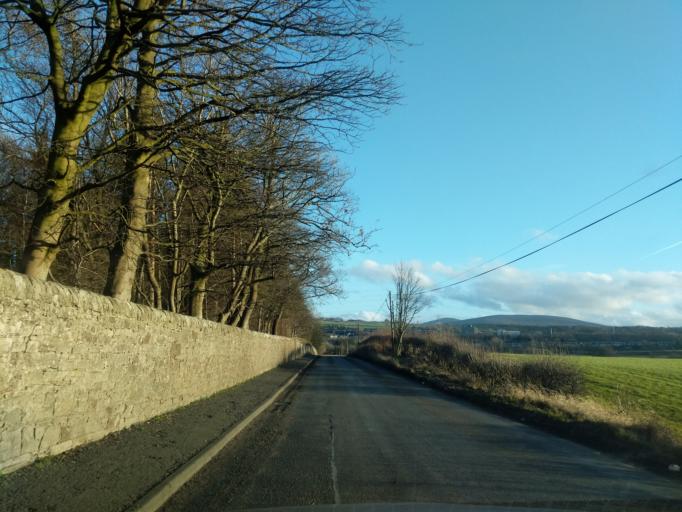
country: GB
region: Scotland
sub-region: Edinburgh
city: Currie
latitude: 55.9042
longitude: -3.3252
